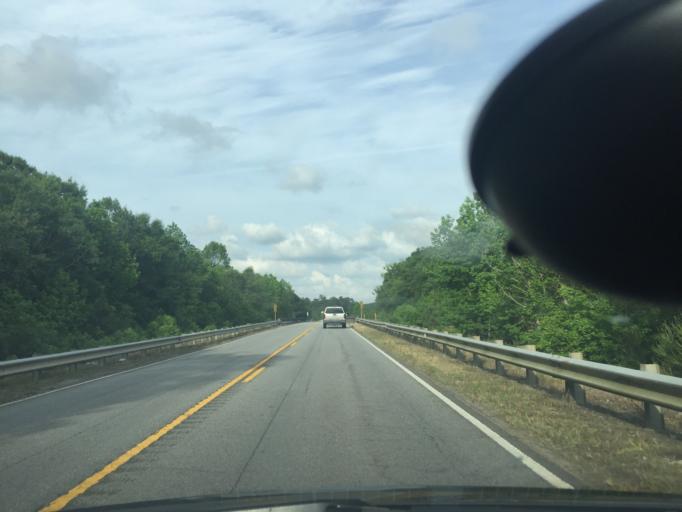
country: US
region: Georgia
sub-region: Chatham County
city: Bloomingdale
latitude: 32.0803
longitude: -81.3813
